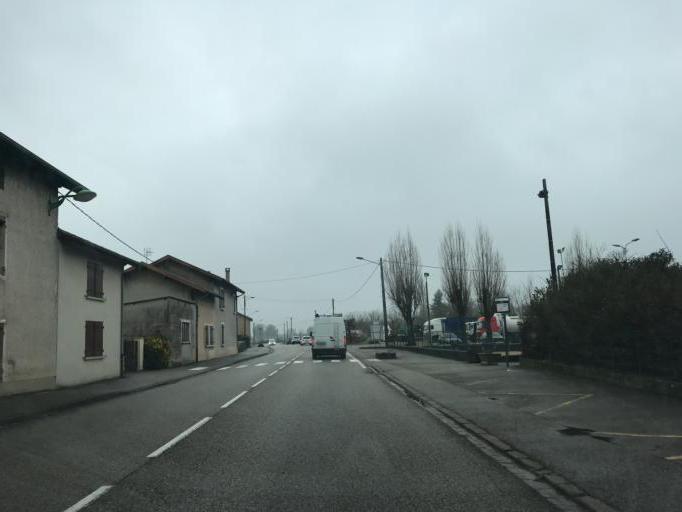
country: FR
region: Rhone-Alpes
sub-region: Departement de l'Ain
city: Servas
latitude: 46.1316
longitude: 5.1638
